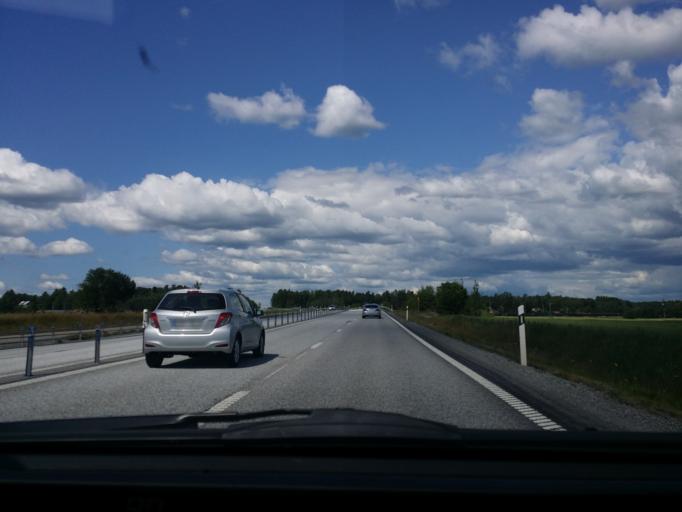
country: SE
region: OErebro
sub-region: Orebro Kommun
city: Hovsta
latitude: 59.3600
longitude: 15.2307
